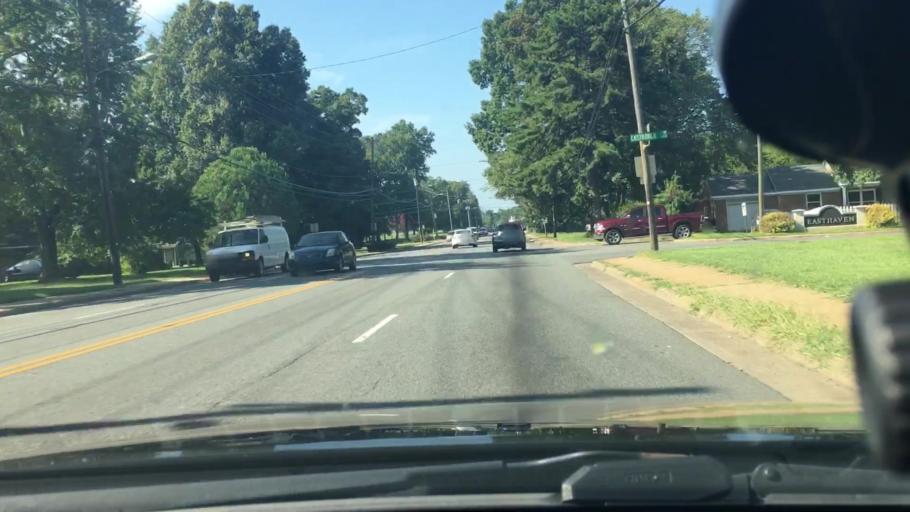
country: US
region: North Carolina
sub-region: Mecklenburg County
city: Matthews
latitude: 35.1919
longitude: -80.7268
